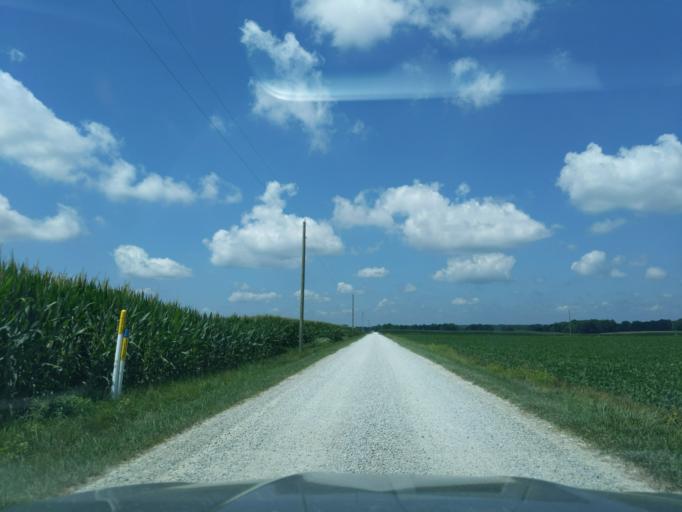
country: US
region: Indiana
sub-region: Ripley County
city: Osgood
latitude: 39.2206
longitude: -85.3726
